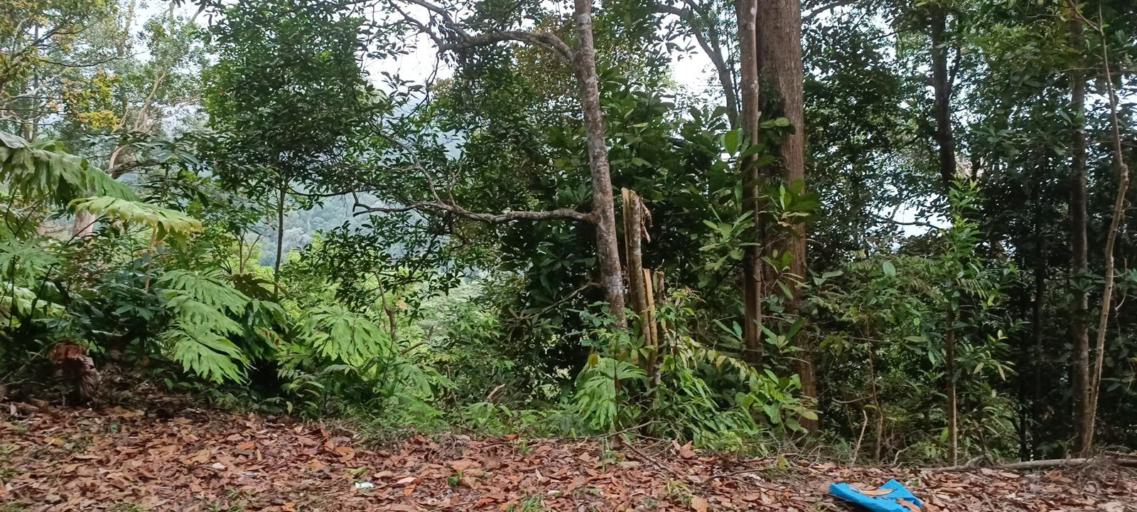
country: MY
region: Perak
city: Taiping
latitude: 4.8656
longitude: 100.7721
